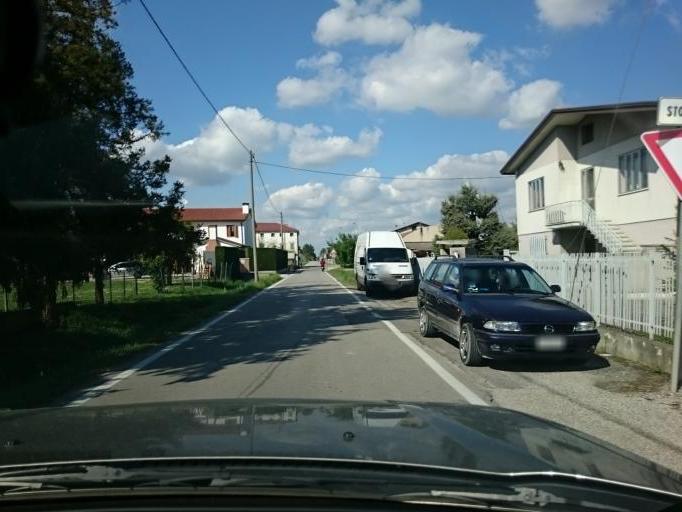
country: IT
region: Veneto
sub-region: Provincia di Padova
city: Villanova
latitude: 45.4862
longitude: 11.9855
